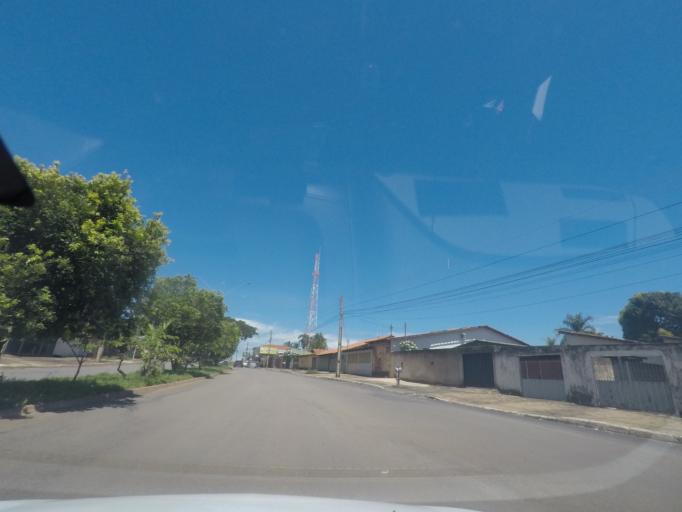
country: BR
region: Goias
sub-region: Aparecida De Goiania
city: Aparecida de Goiania
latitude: -16.7696
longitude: -49.3244
